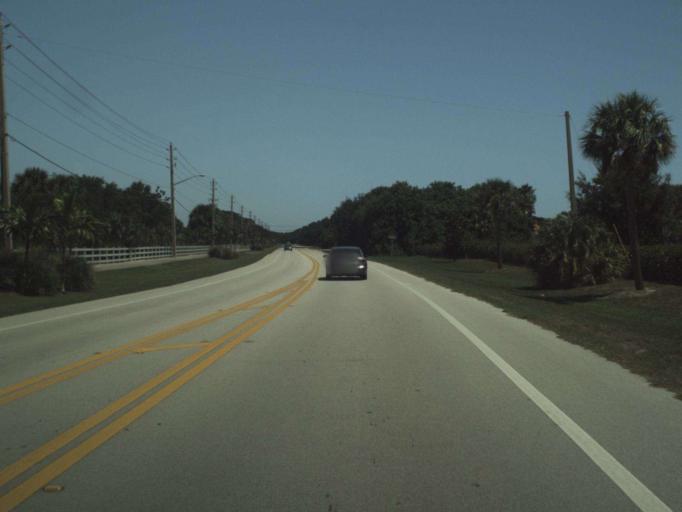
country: US
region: Florida
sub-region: Indian River County
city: South Beach
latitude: 27.5917
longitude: -80.3334
